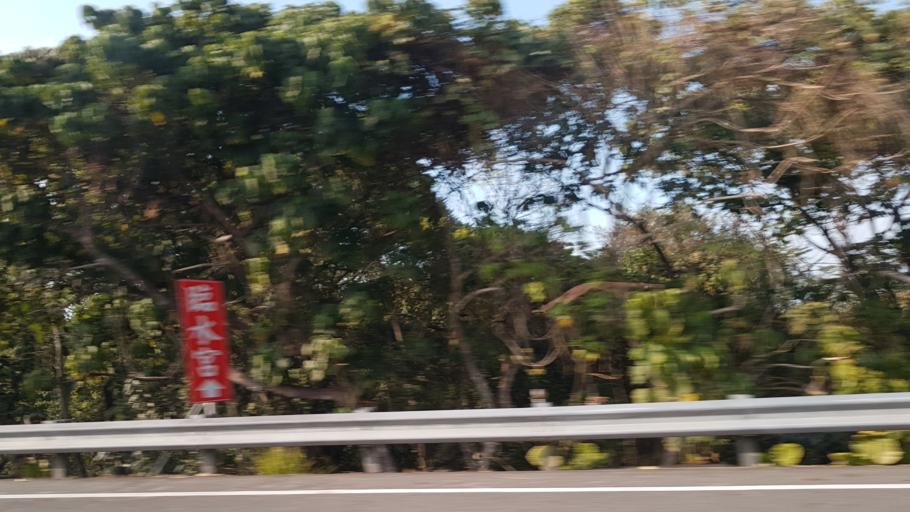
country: TW
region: Taiwan
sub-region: Chiayi
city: Jiayi Shi
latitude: 23.3472
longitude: 120.4368
